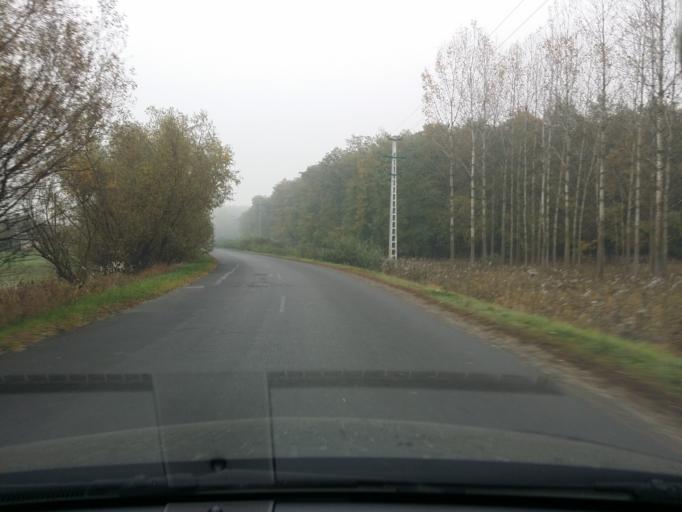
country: HU
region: Szabolcs-Szatmar-Bereg
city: Kek
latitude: 48.0934
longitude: 21.8774
